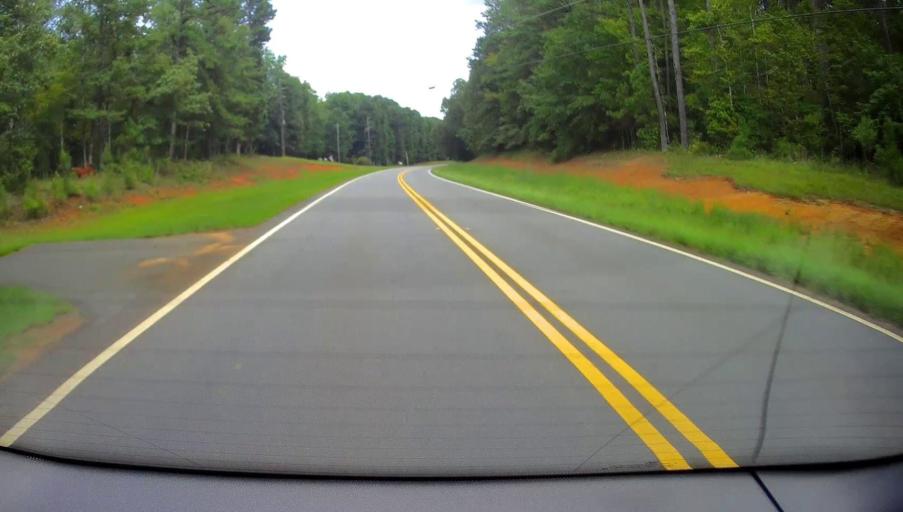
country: US
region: Georgia
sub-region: Monroe County
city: Forsyth
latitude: 32.8826
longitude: -83.9478
